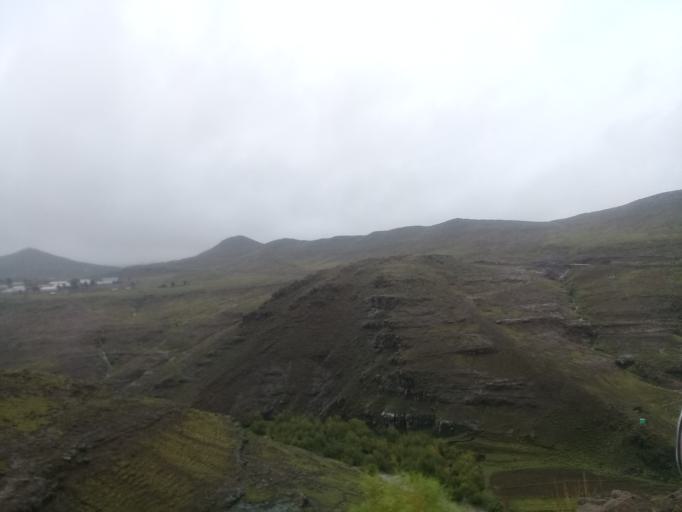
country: LS
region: Mokhotlong
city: Mokhotlong
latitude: -29.3368
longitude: 29.0302
